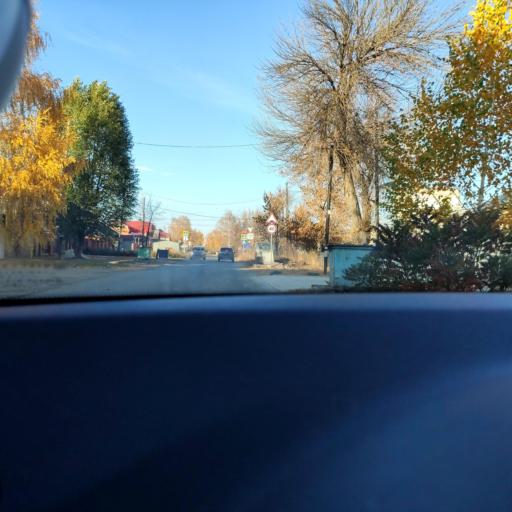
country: RU
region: Samara
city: Petra-Dubrava
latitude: 53.2533
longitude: 50.3289
